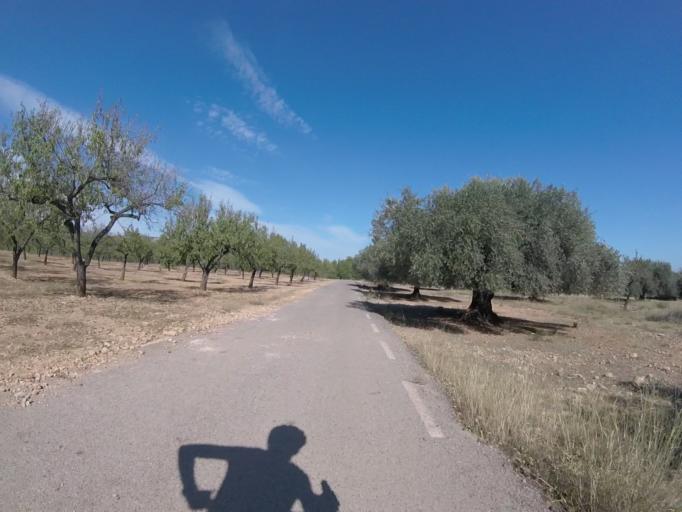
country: ES
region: Valencia
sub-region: Provincia de Castello
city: Sarratella
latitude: 40.2742
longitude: 0.0608
